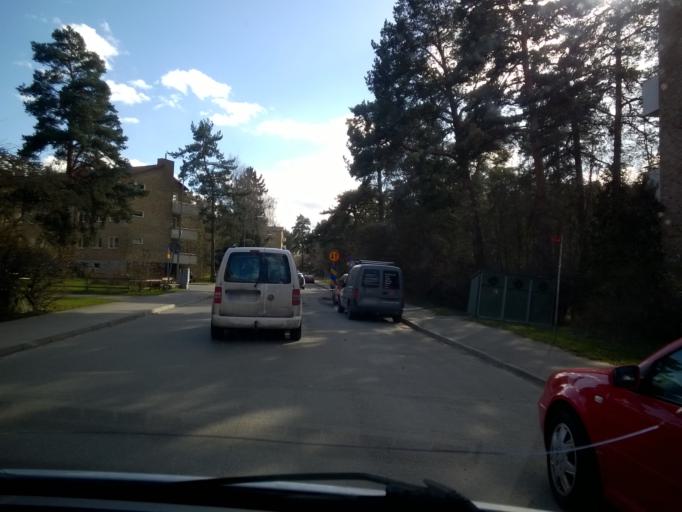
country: SE
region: Stockholm
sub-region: Stockholms Kommun
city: Bromma
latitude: 59.3332
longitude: 17.9495
